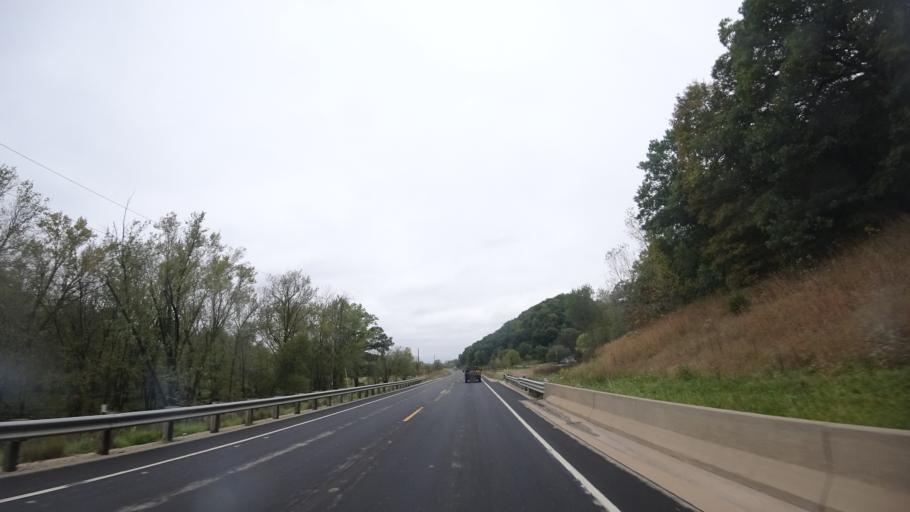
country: US
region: Wisconsin
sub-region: Grant County
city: Boscobel
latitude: 43.1337
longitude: -90.7490
